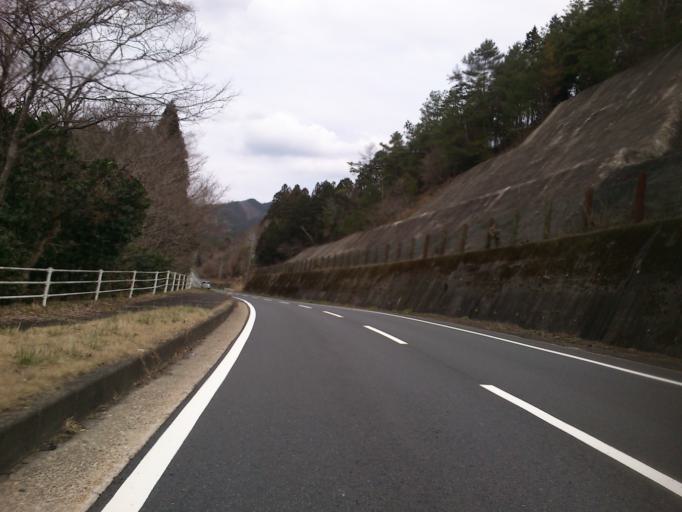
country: JP
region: Kyoto
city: Fukuchiyama
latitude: 35.3870
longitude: 135.0962
